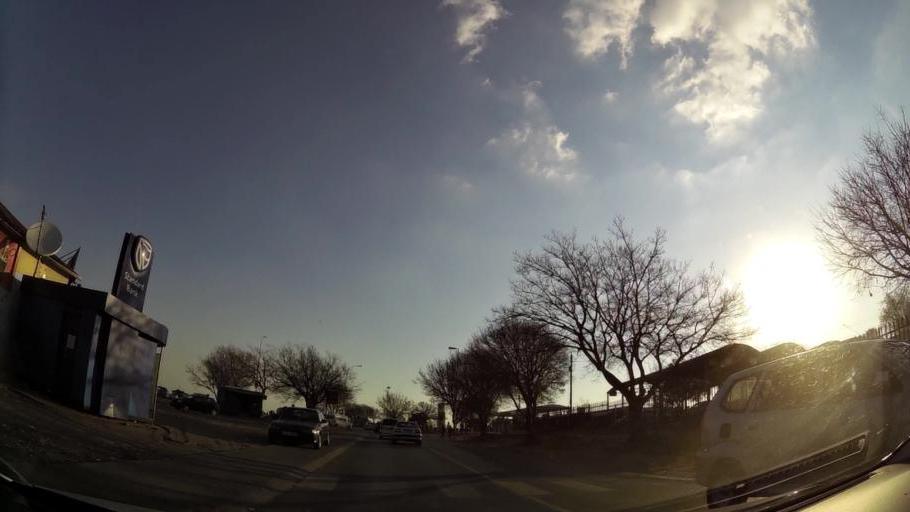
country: ZA
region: Gauteng
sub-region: City of Johannesburg Metropolitan Municipality
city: Midrand
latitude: -26.0213
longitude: 28.1723
